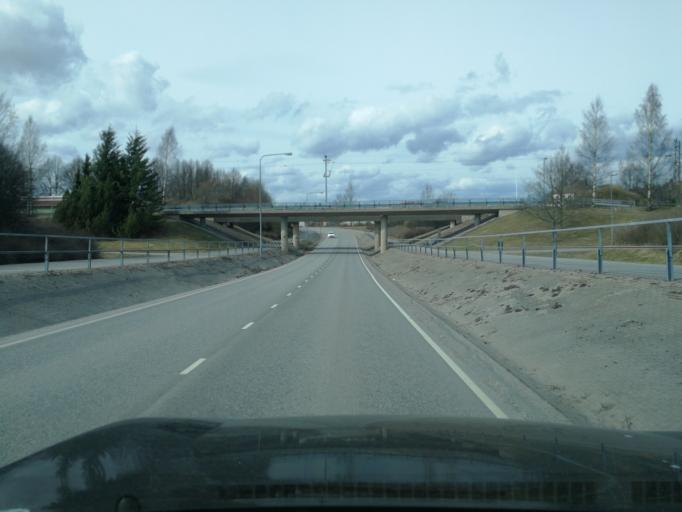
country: FI
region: Uusimaa
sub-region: Helsinki
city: Siuntio
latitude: 60.1402
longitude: 24.2260
